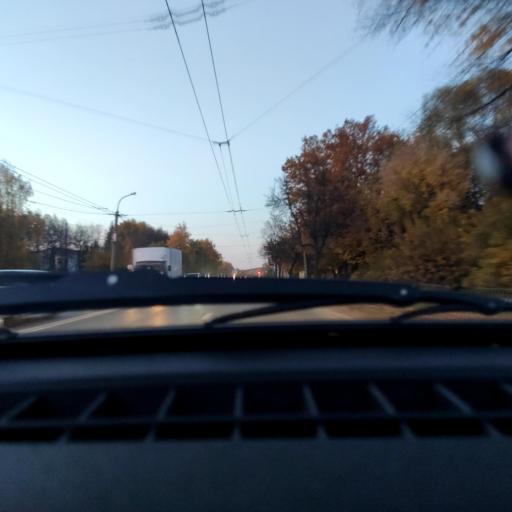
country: RU
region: Bashkortostan
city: Ufa
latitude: 54.7899
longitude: 56.1393
